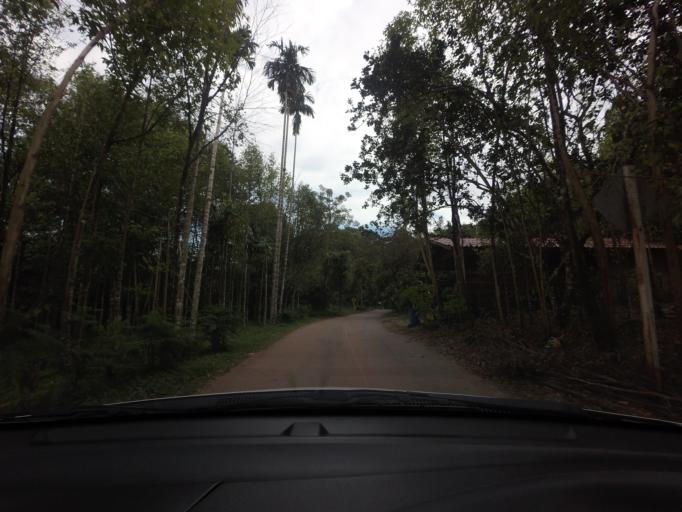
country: TH
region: Nakhon Nayok
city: Nakhon Nayok
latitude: 14.3351
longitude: 101.2857
